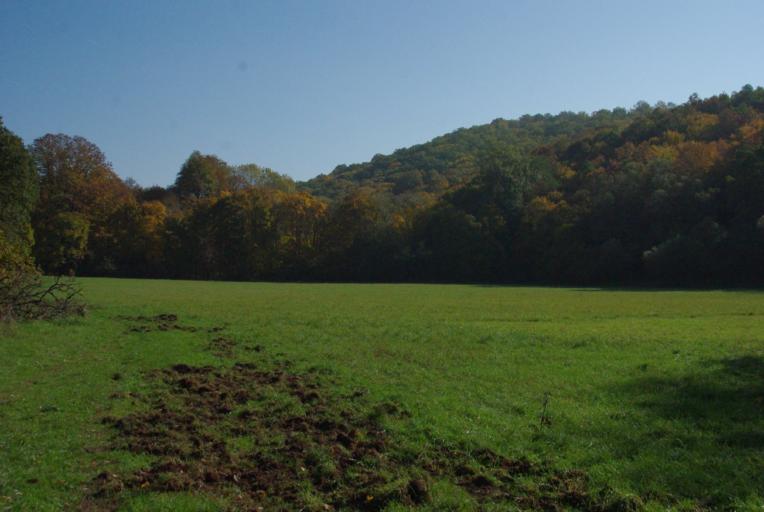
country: HU
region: Pest
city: Szob
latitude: 47.8289
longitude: 18.9195
